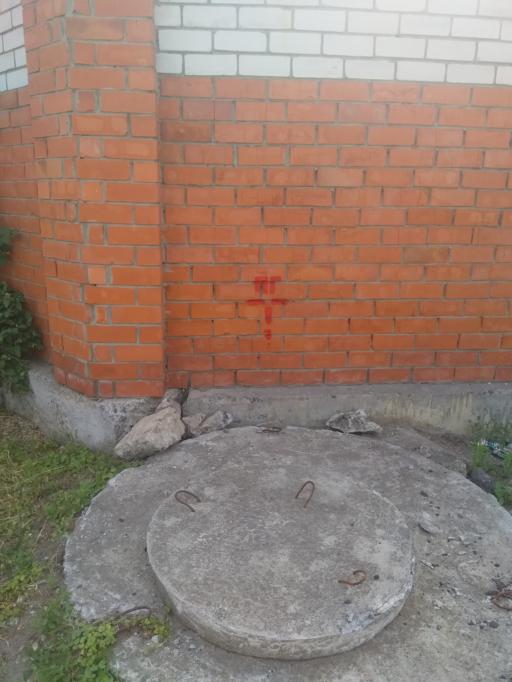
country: RU
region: Voronezj
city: Pridonskoy
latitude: 51.6439
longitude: 39.0848
